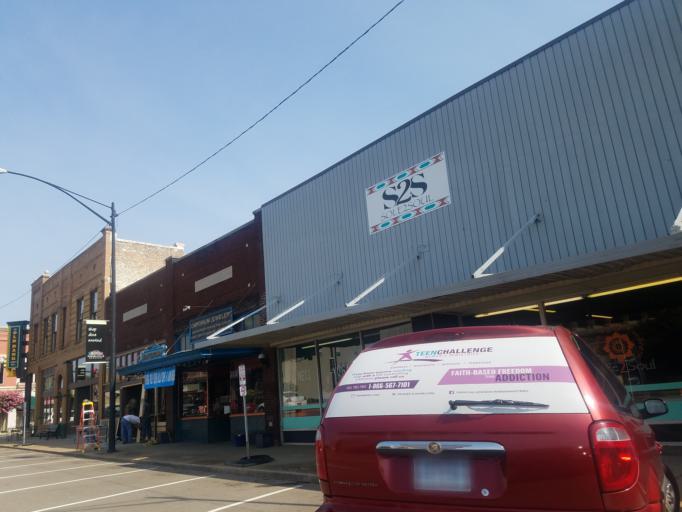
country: US
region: Arkansas
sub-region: Pope County
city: Russellville
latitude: 35.2784
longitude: -93.1348
